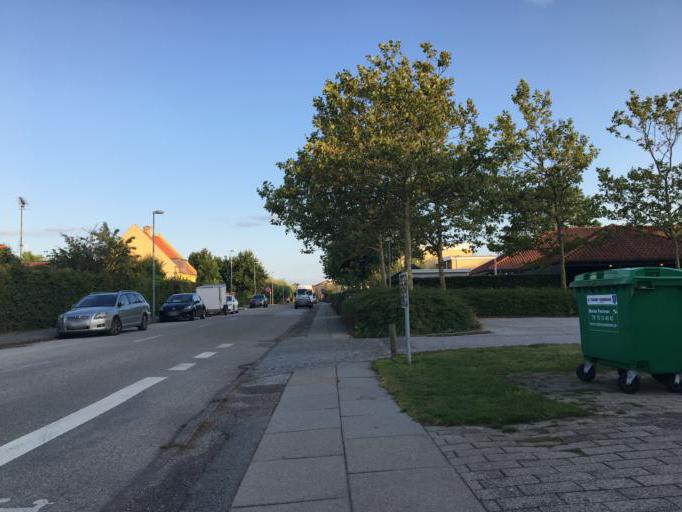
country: DK
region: Capital Region
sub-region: Tarnby Kommune
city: Tarnby
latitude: 55.6429
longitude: 12.6353
